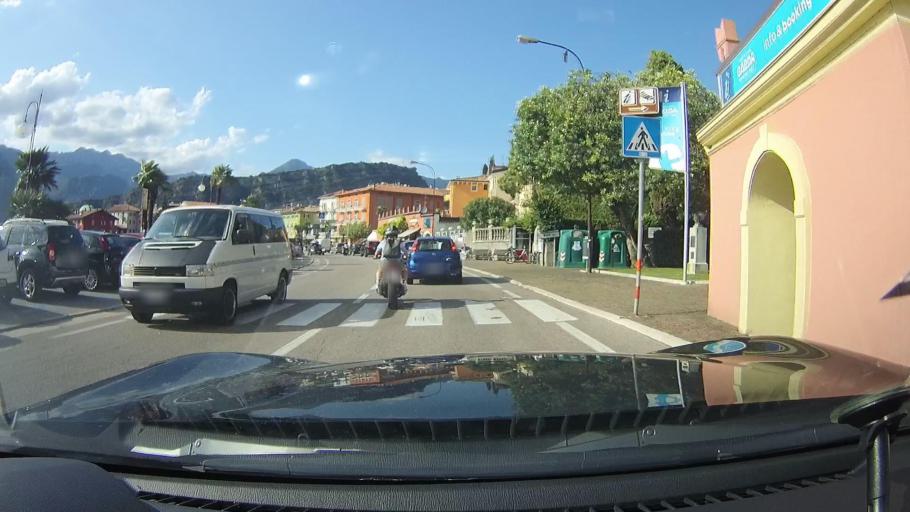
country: IT
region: Trentino-Alto Adige
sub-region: Provincia di Trento
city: Torbole sul Garda
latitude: 45.8677
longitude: 10.8771
